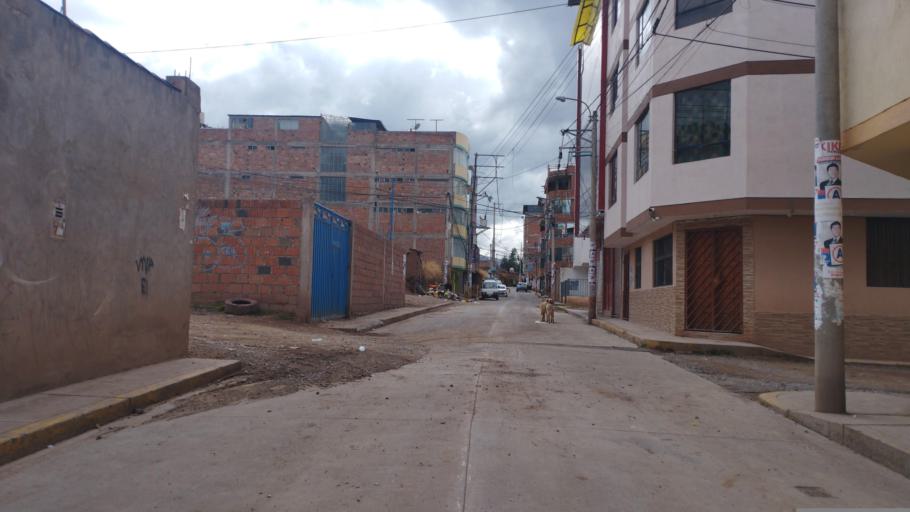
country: PE
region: Cusco
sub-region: Provincia de Cusco
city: Cusco
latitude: -13.5246
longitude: -71.9410
